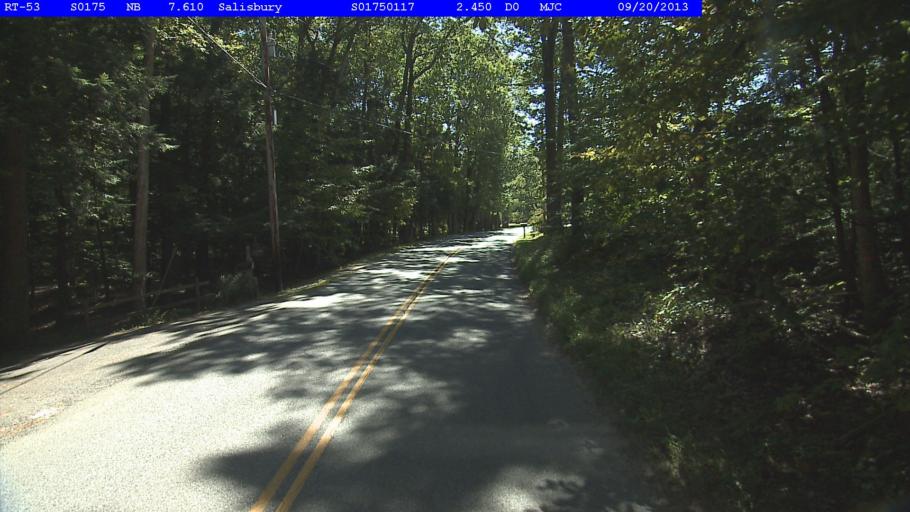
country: US
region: Vermont
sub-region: Rutland County
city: Brandon
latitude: 43.9230
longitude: -73.0817
